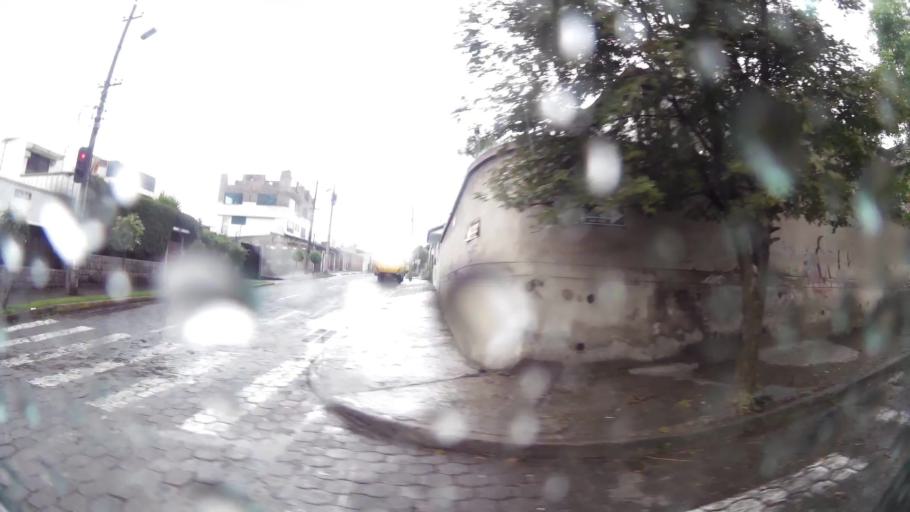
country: EC
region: Pichincha
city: Quito
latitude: -0.1571
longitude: -78.4644
